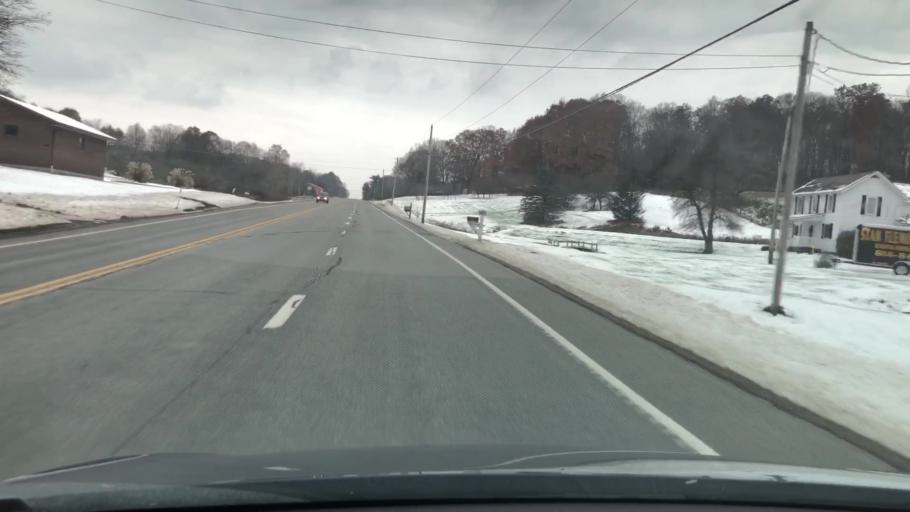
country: US
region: Pennsylvania
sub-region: Jefferson County
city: Brookville
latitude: 41.1494
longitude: -79.1253
